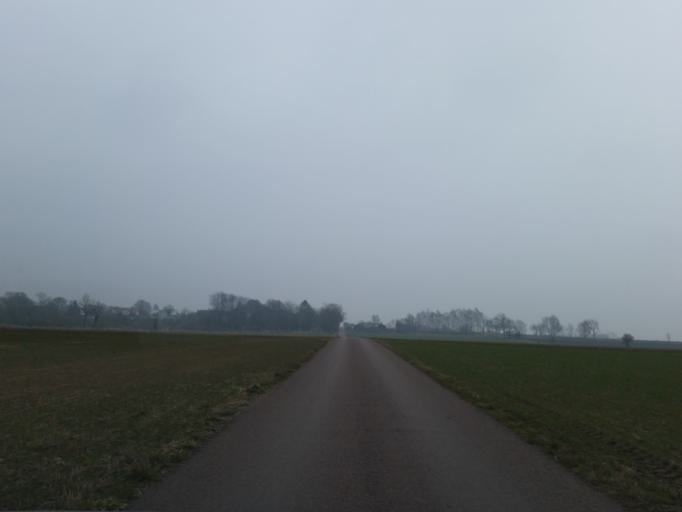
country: SE
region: Kalmar
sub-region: Morbylanga Kommun
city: Moerbylanga
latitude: 56.4410
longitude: 16.4153
